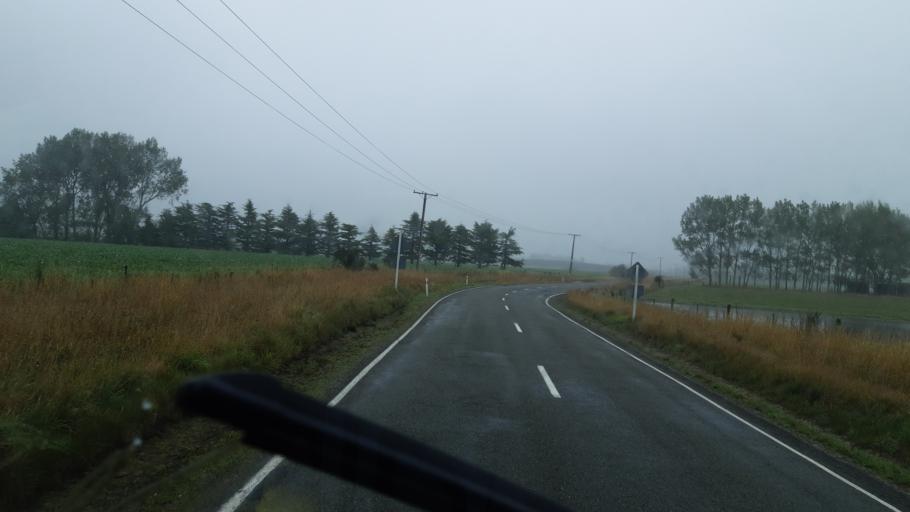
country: NZ
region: Otago
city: Oamaru
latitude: -44.9273
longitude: 170.8113
